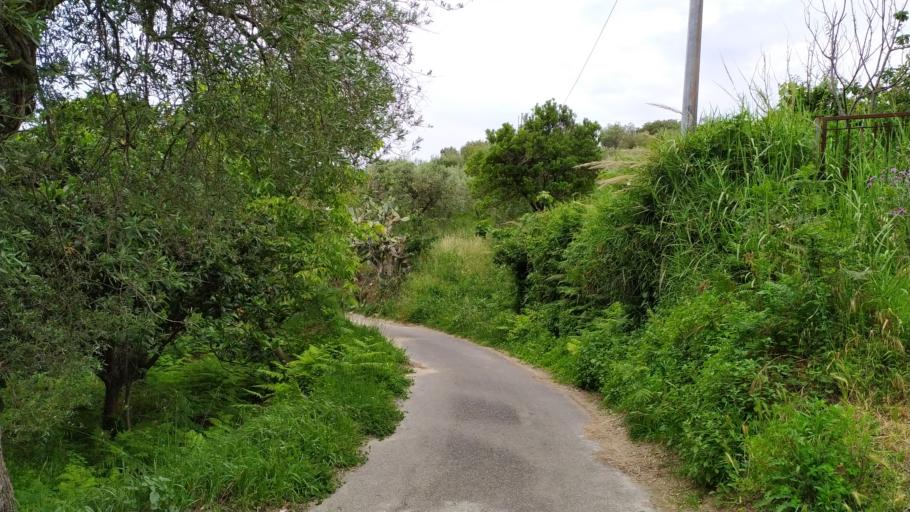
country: IT
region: Sicily
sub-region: Messina
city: Gualtieri Sicamino
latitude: 38.1550
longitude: 15.3008
